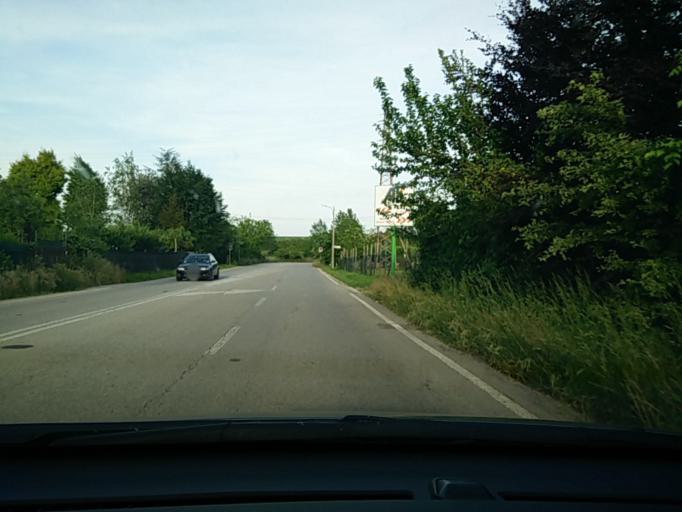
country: IT
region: Veneto
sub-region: Provincia di Padova
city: Vigodarzere
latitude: 45.4373
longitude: 11.8630
